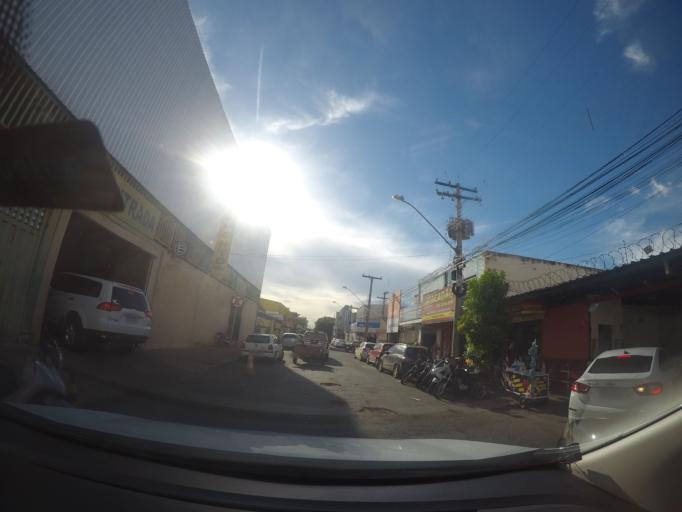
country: BR
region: Goias
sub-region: Goiania
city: Goiania
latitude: -16.6743
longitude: -49.2857
